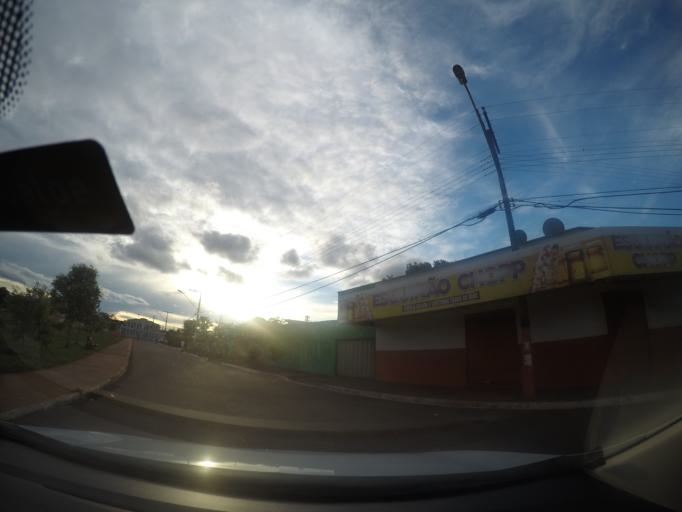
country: BR
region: Goias
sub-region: Goianira
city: Goianira
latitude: -16.5866
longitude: -49.3703
